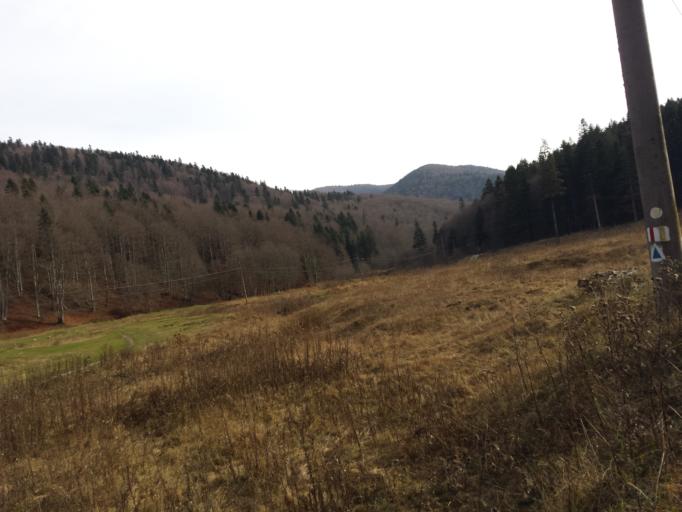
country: RO
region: Prahova
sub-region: Oras Azuga
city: Azuga
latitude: 45.4315
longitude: 25.5313
